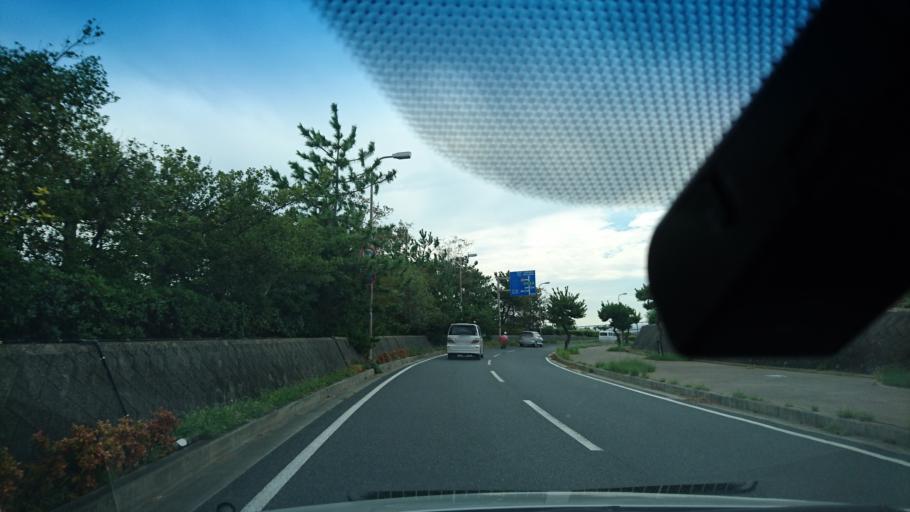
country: JP
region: Hyogo
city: Ashiya
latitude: 34.7161
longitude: 135.3077
